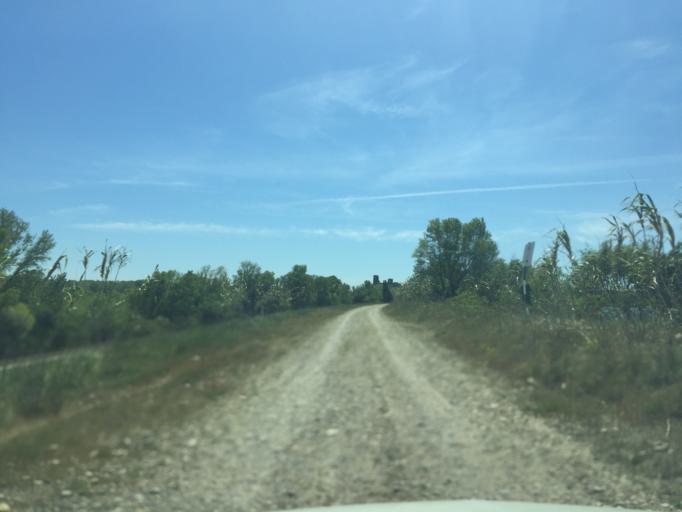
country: FR
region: Languedoc-Roussillon
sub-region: Departement du Gard
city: Roquemaure
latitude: 44.0625
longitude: 4.7913
